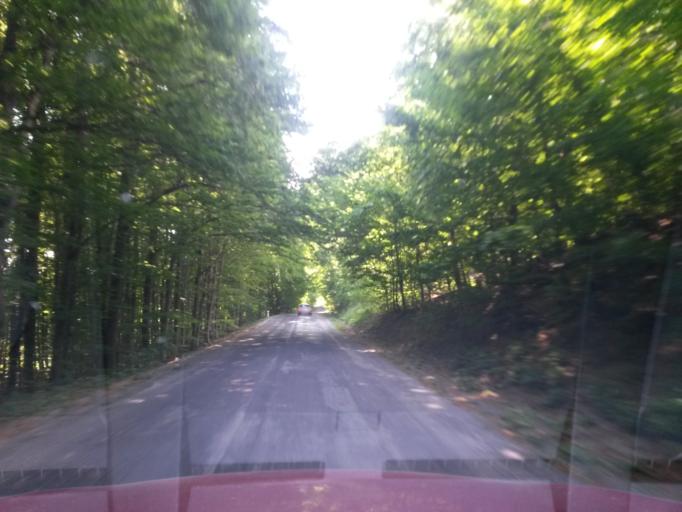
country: SK
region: Kosicky
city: Moldava nad Bodvou
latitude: 48.7284
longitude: 21.0333
